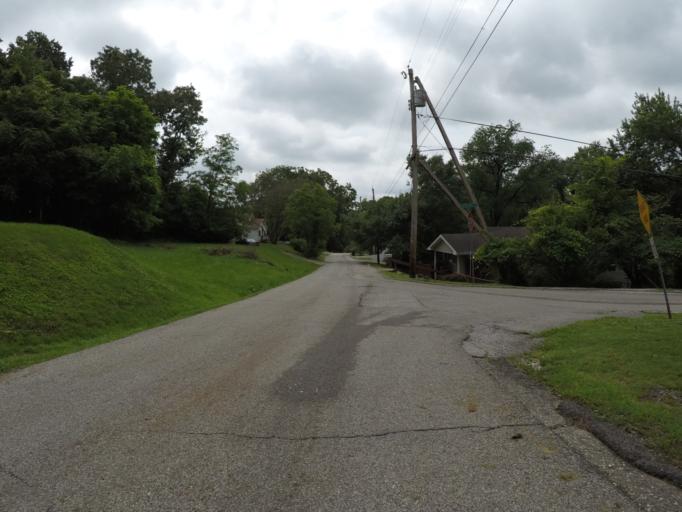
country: US
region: West Virginia
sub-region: Cabell County
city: Huntington
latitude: 38.4133
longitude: -82.3964
